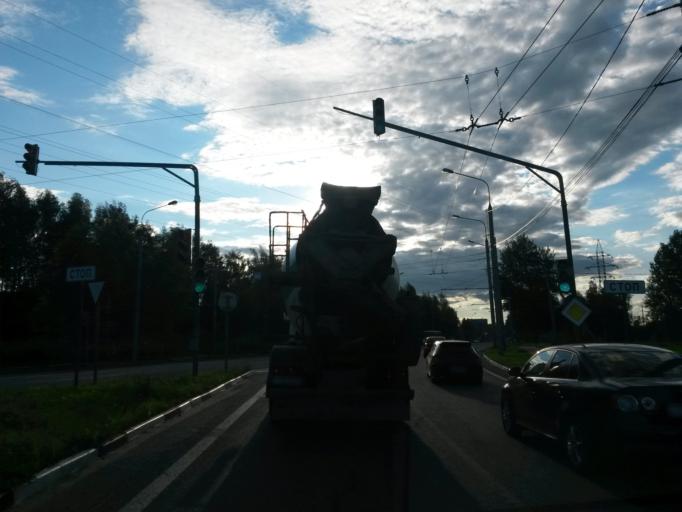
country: RU
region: Jaroslavl
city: Yaroslavl
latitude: 57.6724
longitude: 39.8308
